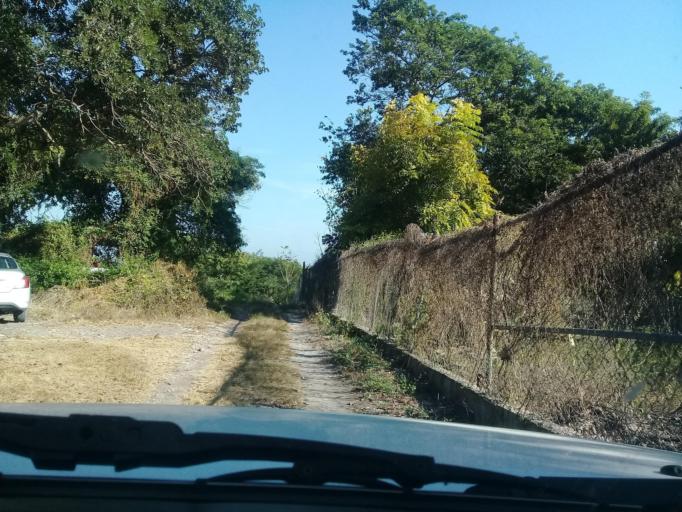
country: MX
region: Veracruz
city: Rinconada
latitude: 19.4019
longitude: -96.5599
